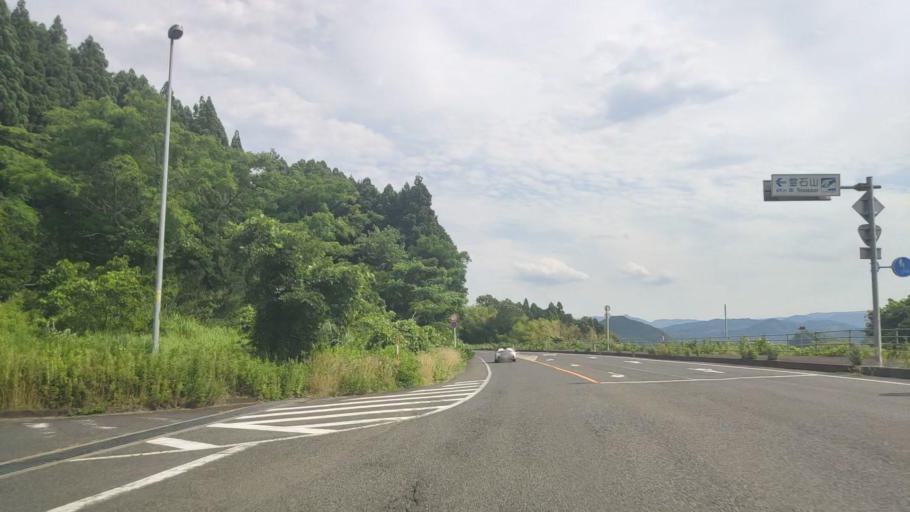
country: JP
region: Tottori
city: Tottori
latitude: 35.4121
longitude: 134.2064
